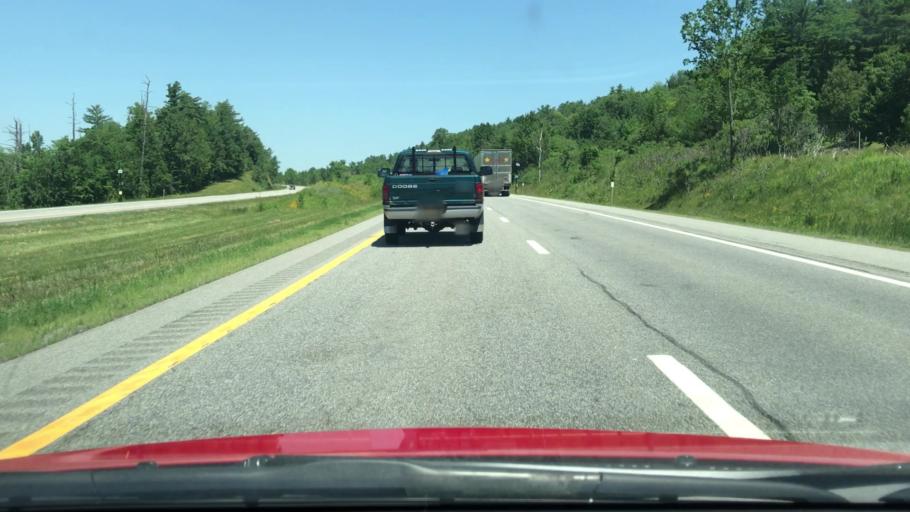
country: US
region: New York
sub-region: Essex County
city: Keeseville
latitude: 44.4266
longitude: -73.4920
